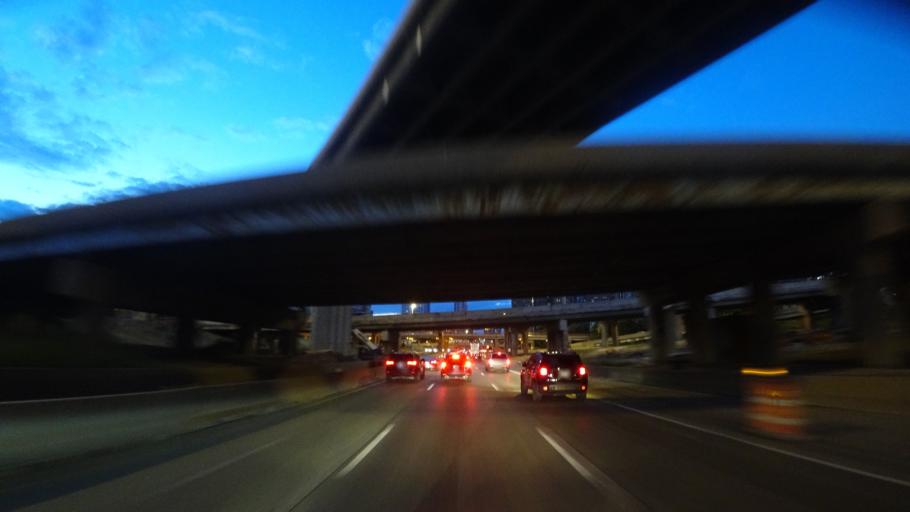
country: US
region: Illinois
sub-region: Cook County
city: Chicago
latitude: 41.8753
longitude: -87.6452
